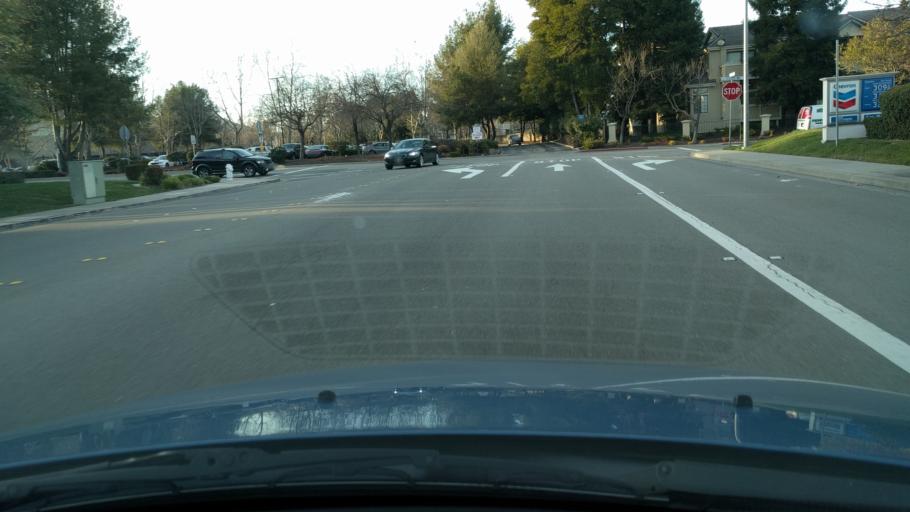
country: US
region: California
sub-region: Contra Costa County
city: San Ramon
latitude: 37.7818
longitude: -121.9704
